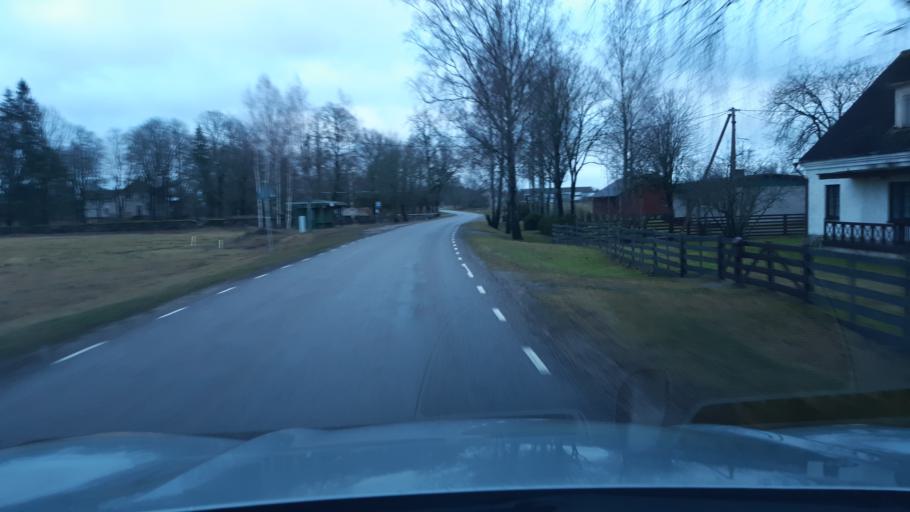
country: EE
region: Raplamaa
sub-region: Kohila vald
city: Kohila
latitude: 59.1168
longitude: 24.6810
